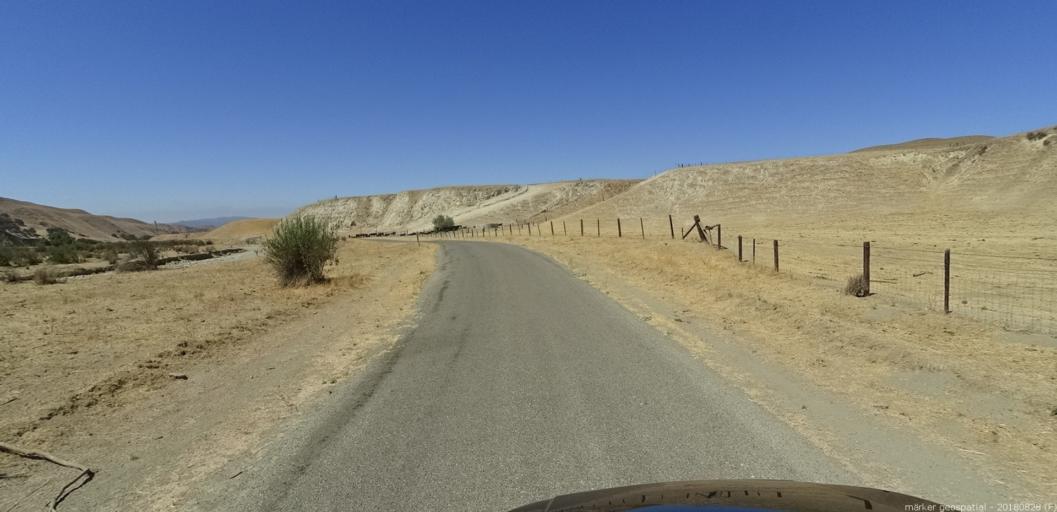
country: US
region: California
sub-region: San Luis Obispo County
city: San Miguel
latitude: 36.0462
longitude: -120.8266
